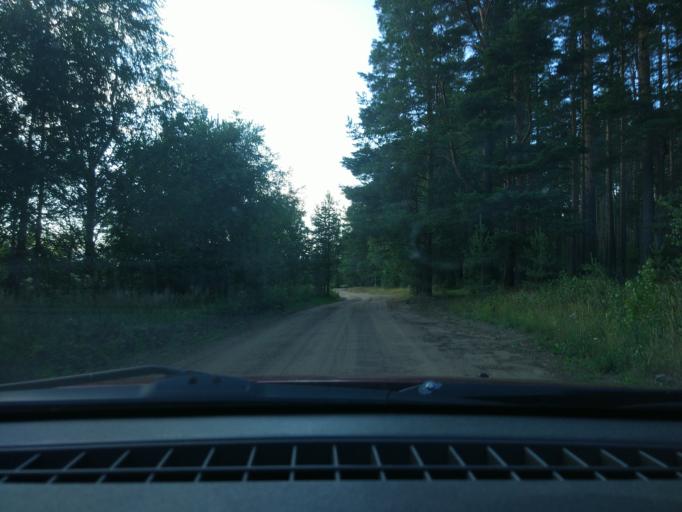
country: RU
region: Leningrad
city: Priozersk
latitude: 60.9330
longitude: 30.0503
